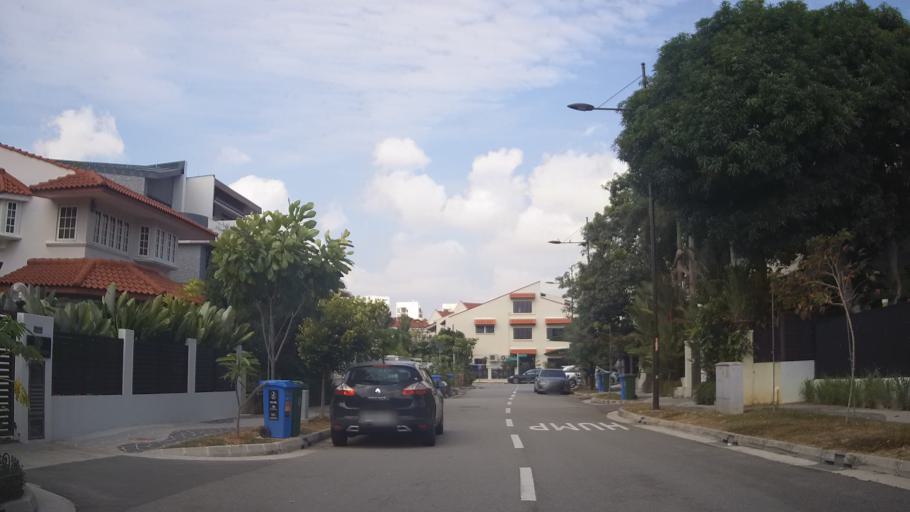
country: SG
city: Singapore
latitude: 1.3225
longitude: 103.9505
